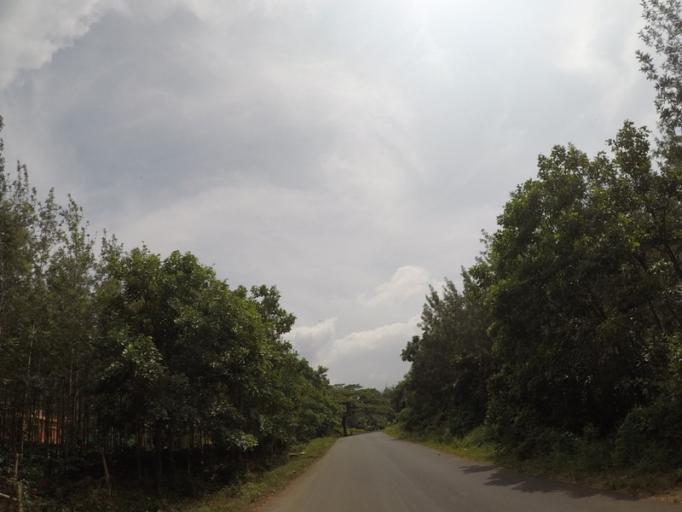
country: IN
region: Karnataka
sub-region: Chikmagalur
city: Chikmagalur
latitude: 13.4066
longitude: 75.7967
